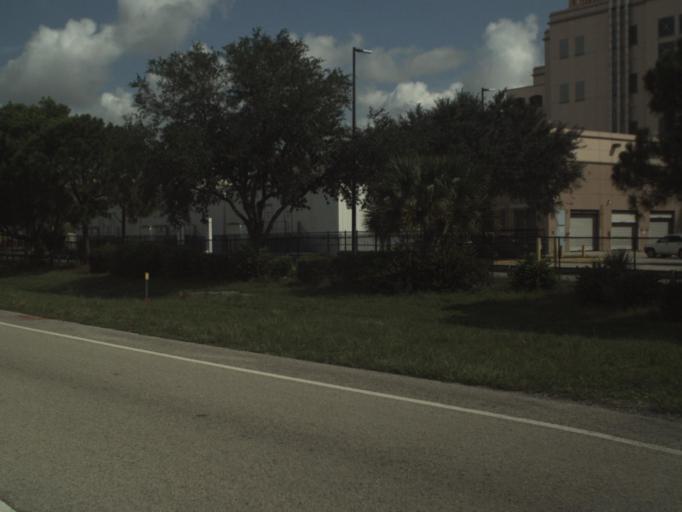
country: US
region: Florida
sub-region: Palm Beach County
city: North Palm Beach
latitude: 26.7839
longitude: -80.1133
